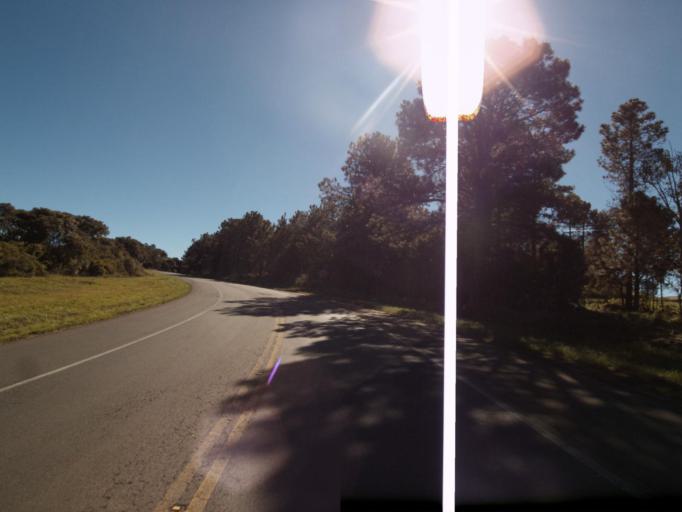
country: BR
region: Santa Catarina
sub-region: Joacaba
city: Joacaba
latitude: -27.1161
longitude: -51.6310
